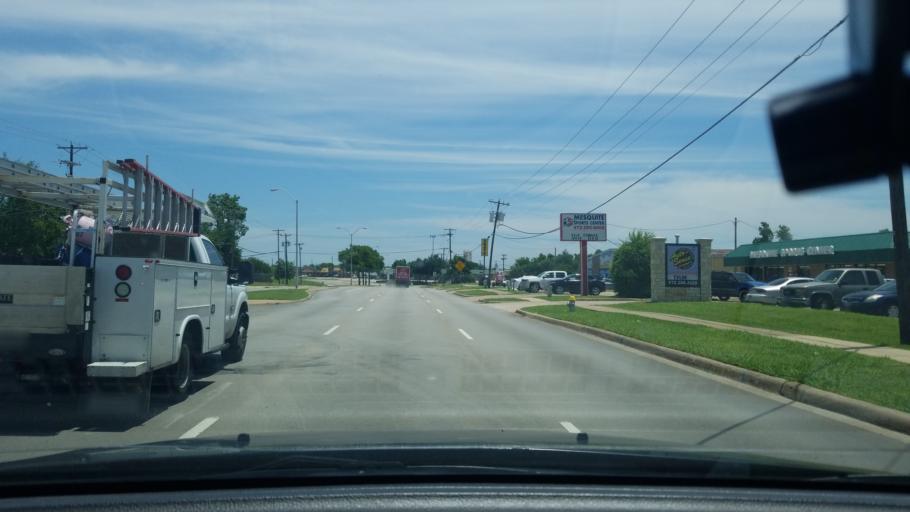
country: US
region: Texas
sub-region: Dallas County
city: Mesquite
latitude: 32.7727
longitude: -96.6145
